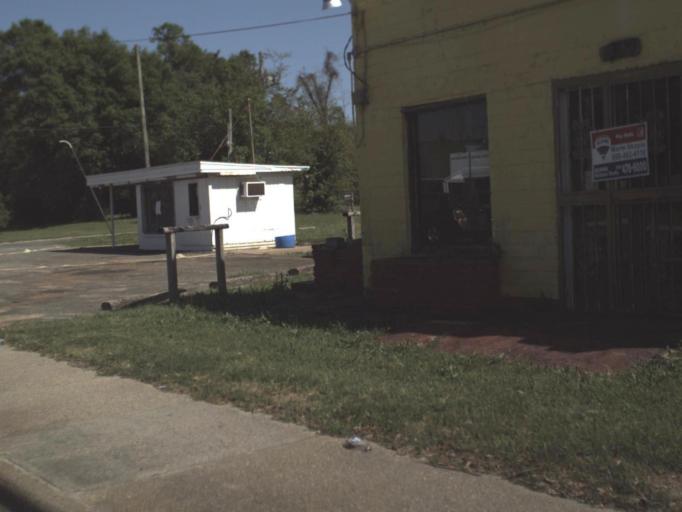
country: US
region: Florida
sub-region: Escambia County
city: Pensacola
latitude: 30.4203
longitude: -87.2328
